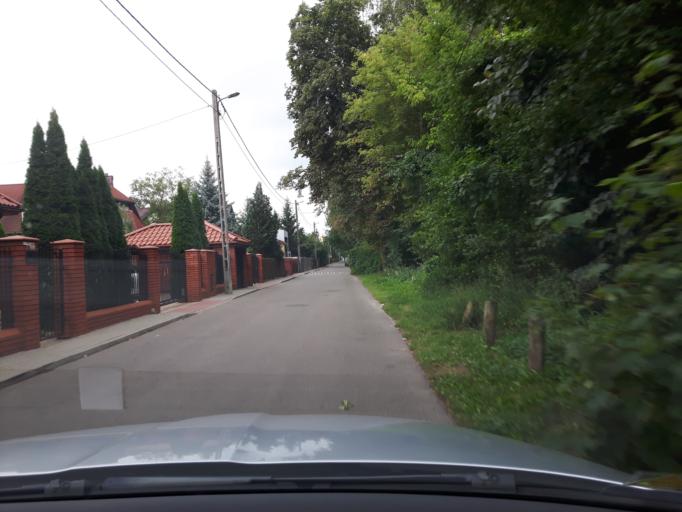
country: PL
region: Masovian Voivodeship
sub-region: Warszawa
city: Praga Poludnie
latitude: 52.2502
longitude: 21.1237
